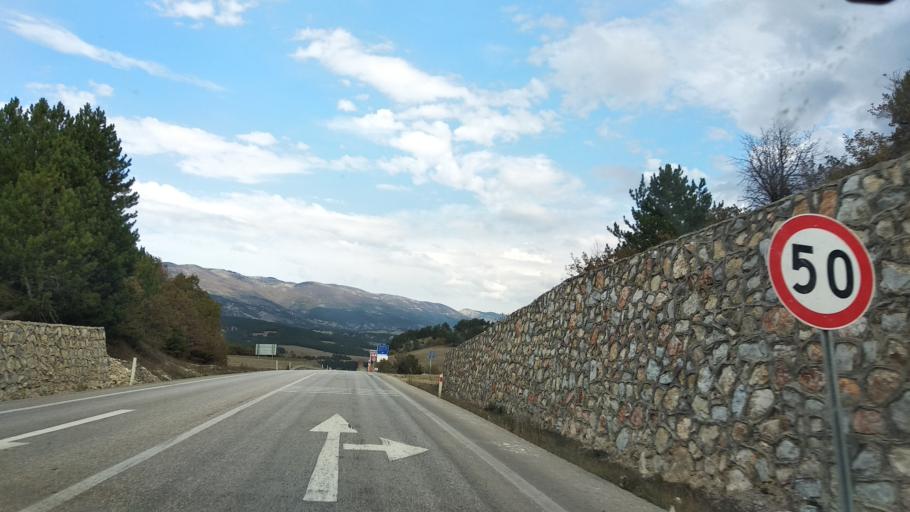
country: TR
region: Bolu
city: Mudurnu
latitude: 40.4771
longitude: 31.1571
